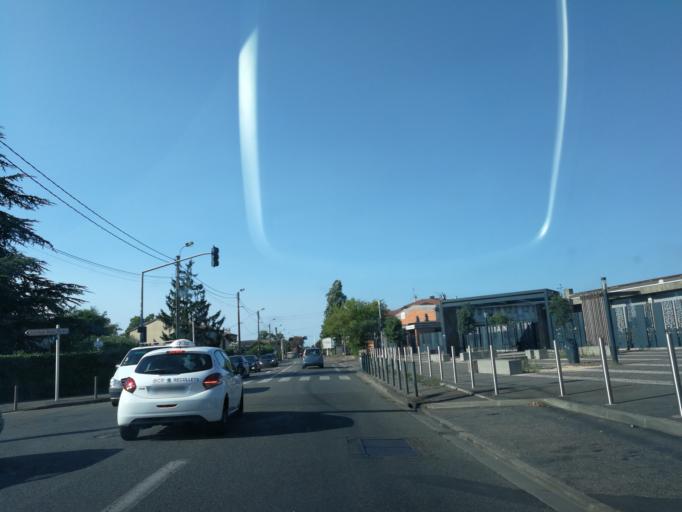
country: FR
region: Midi-Pyrenees
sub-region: Departement de la Haute-Garonne
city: Aucamville
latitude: 43.6393
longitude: 1.4393
